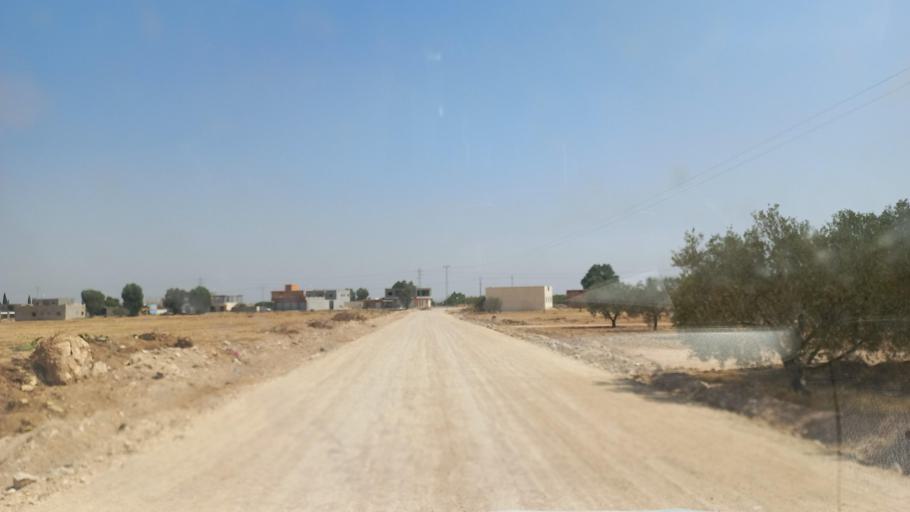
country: TN
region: Al Qasrayn
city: Kasserine
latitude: 35.2555
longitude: 9.0152
